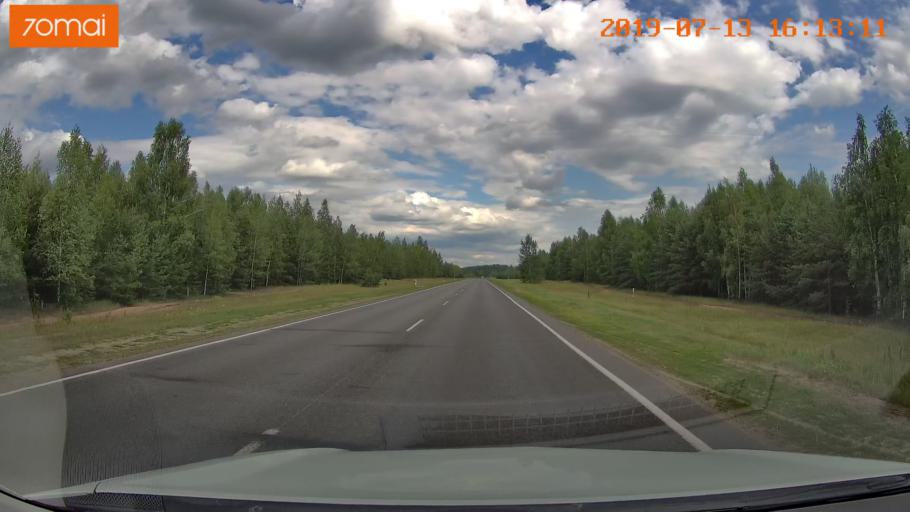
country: BY
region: Mogilev
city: Babruysk
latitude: 53.1640
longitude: 29.2974
